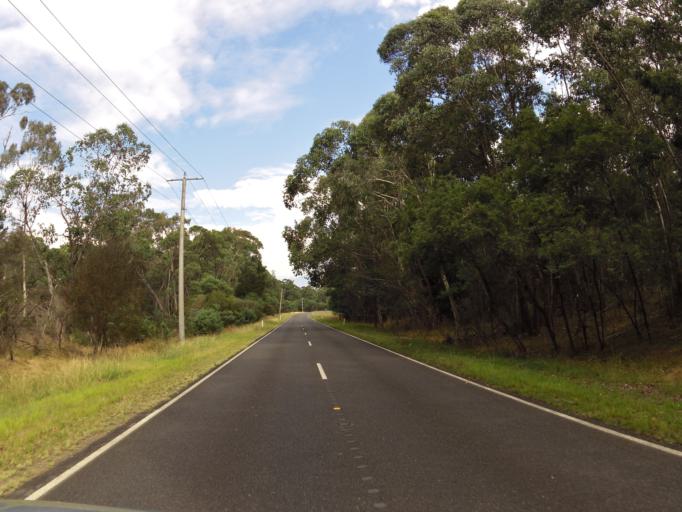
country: AU
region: Victoria
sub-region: Alpine
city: Mount Beauty
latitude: -36.7556
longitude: 147.0204
